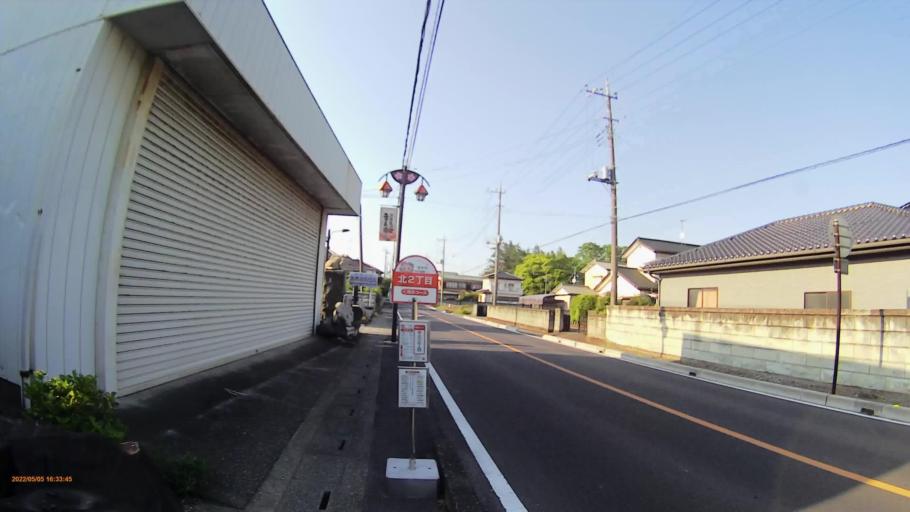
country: JP
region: Saitama
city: Satte
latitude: 36.0863
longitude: 139.7214
